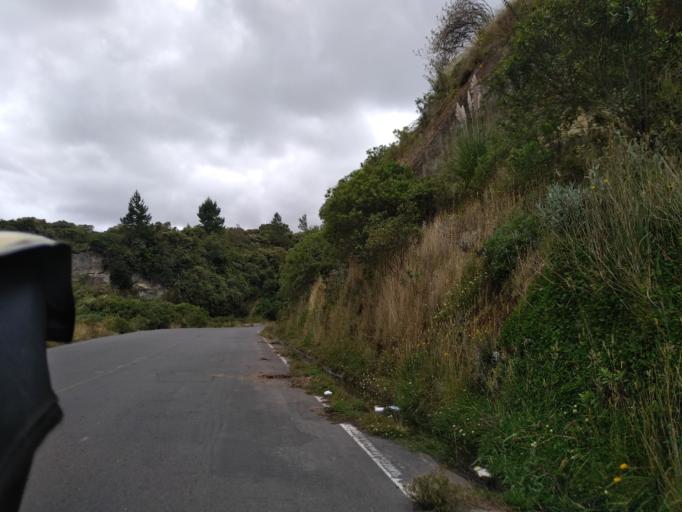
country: EC
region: Cotopaxi
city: Saquisili
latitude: -0.7130
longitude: -78.7629
